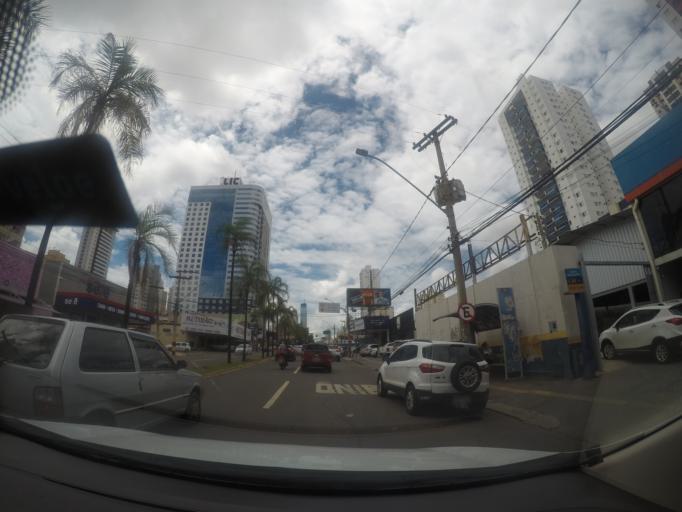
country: BR
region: Goias
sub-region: Goiania
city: Goiania
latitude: -16.6892
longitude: -49.2765
